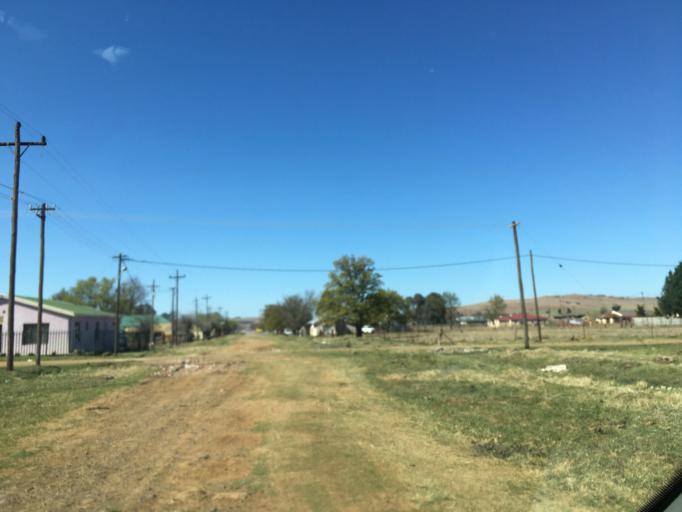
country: ZA
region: Eastern Cape
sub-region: Chris Hani District Municipality
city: Elliot
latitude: -31.3298
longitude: 27.8448
